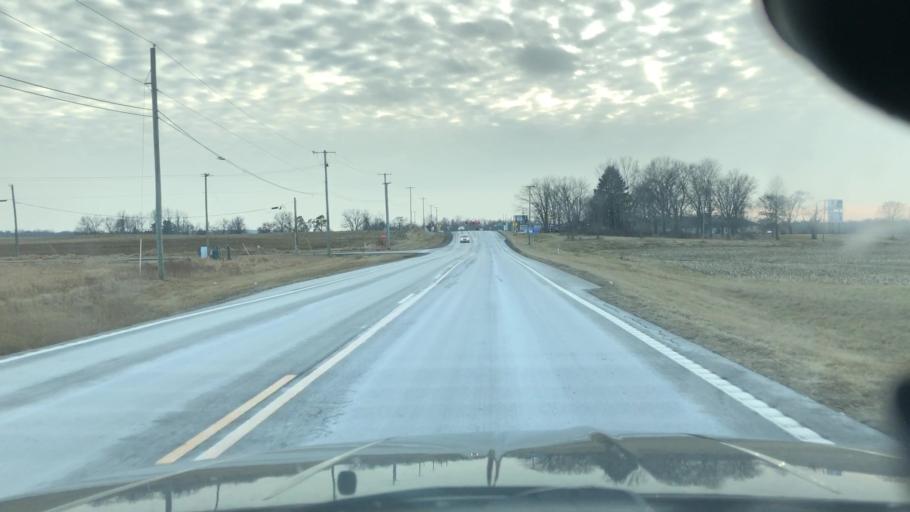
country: US
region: Ohio
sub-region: Wayne County
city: Rittman
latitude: 40.9285
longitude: -81.7601
